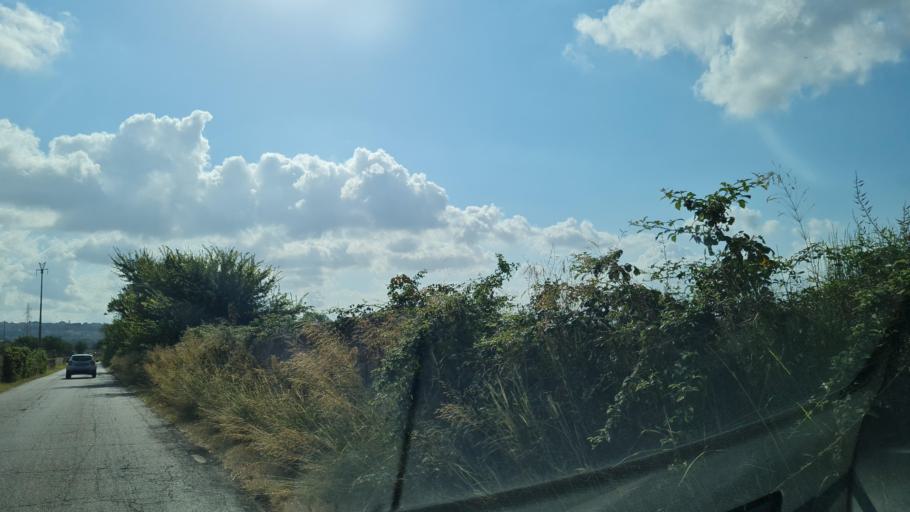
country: IT
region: Latium
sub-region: Provincia di Viterbo
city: Tarquinia
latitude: 42.2538
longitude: 11.7252
